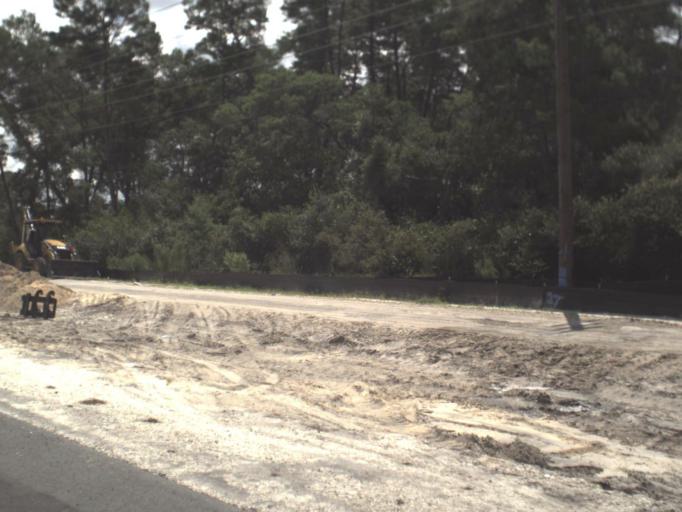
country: US
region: Florida
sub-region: Hernando County
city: North Weeki Wachee
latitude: 28.5217
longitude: -82.5629
